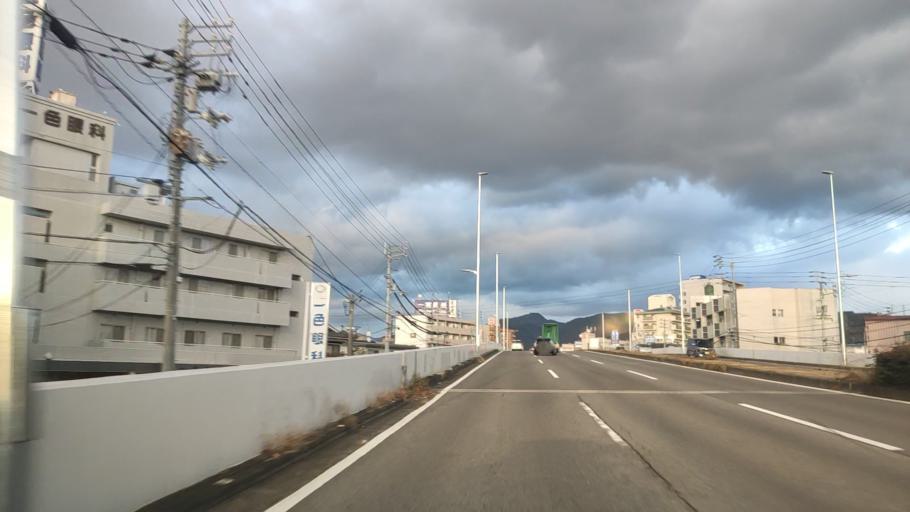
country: JP
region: Ehime
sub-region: Shikoku-chuo Shi
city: Matsuyama
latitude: 33.8246
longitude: 132.7800
